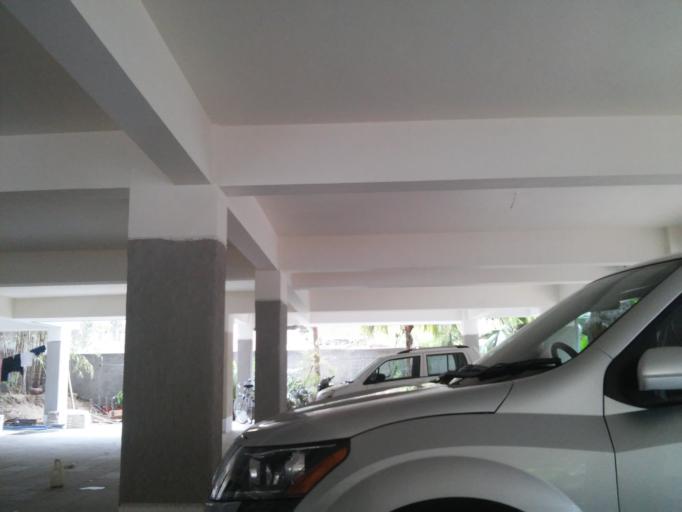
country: IN
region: Gujarat
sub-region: Ahmadabad
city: Ahmedabad
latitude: 23.0157
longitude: 72.5643
